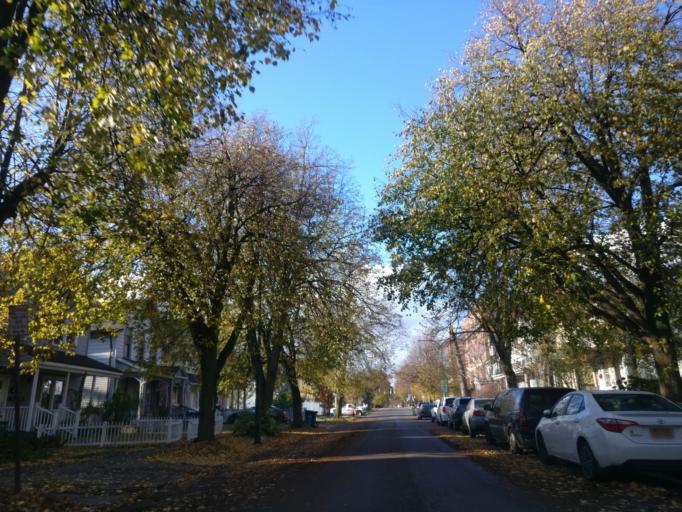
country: US
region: New York
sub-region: Erie County
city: Buffalo
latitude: 42.8993
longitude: -78.8920
